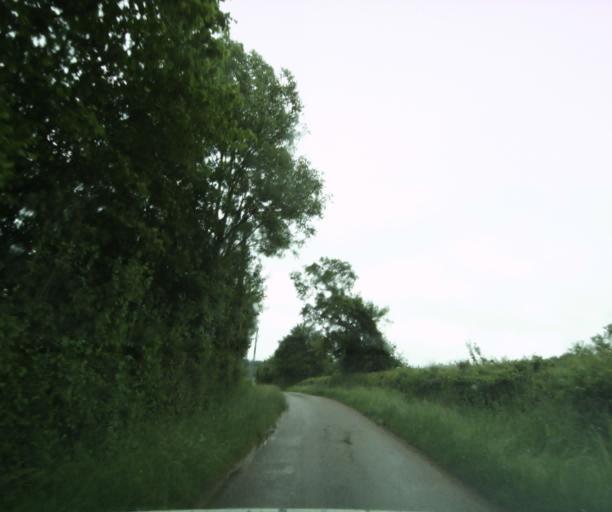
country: FR
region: Bourgogne
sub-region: Departement de Saone-et-Loire
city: Charolles
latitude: 46.4886
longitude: 4.2879
